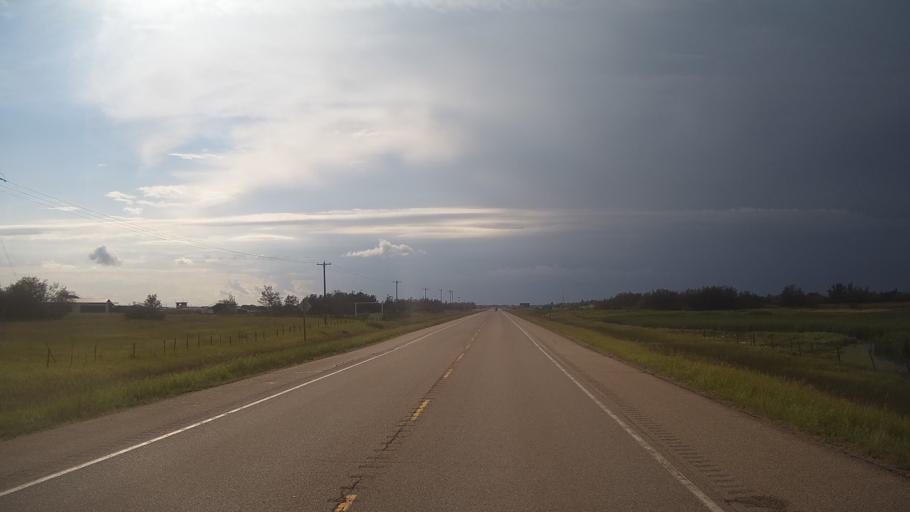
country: CA
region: Alberta
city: Viking
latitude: 53.1647
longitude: -112.0206
